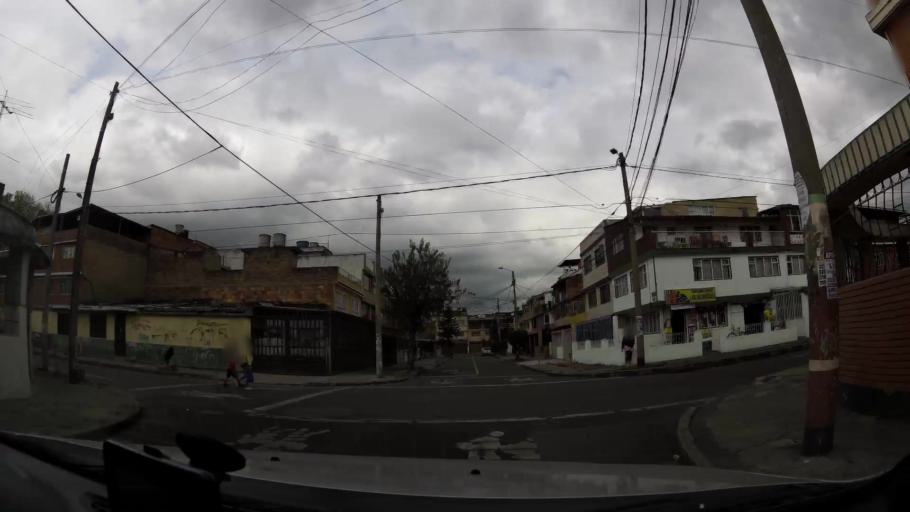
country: CO
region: Bogota D.C.
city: Bogota
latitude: 4.6179
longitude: -74.1169
